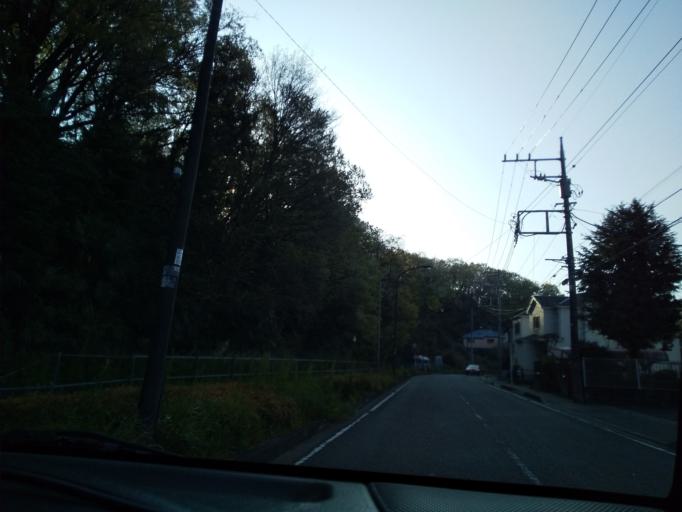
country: JP
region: Kanagawa
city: Zama
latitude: 35.5563
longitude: 139.3655
